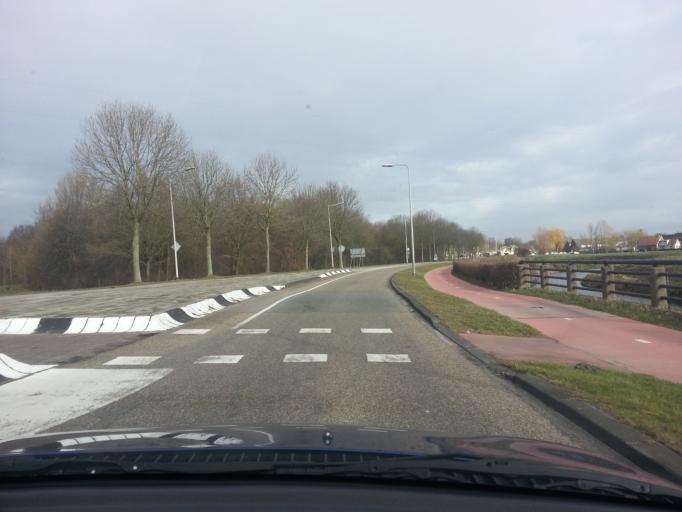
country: NL
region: South Holland
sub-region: Gemeente Spijkenisse
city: Spijkenisse
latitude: 51.8273
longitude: 4.3337
